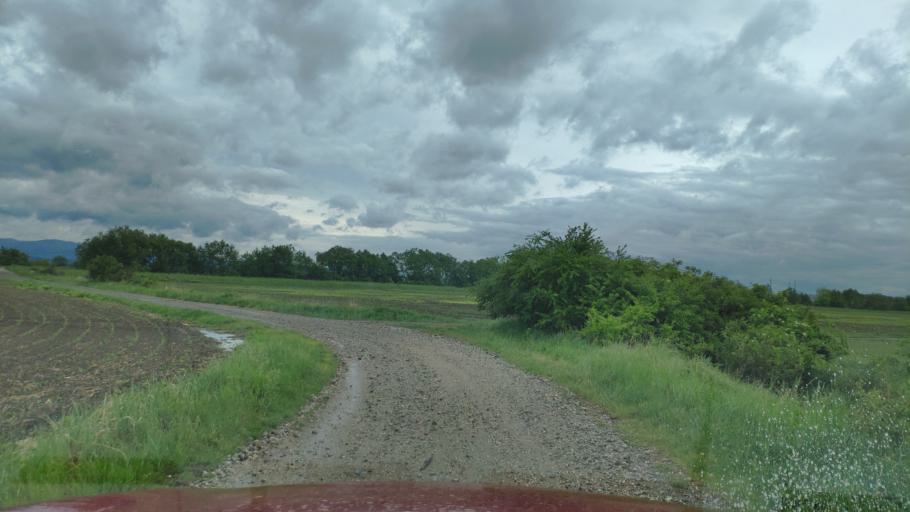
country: SK
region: Kosicky
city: Moldava nad Bodvou
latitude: 48.5553
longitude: 21.1163
